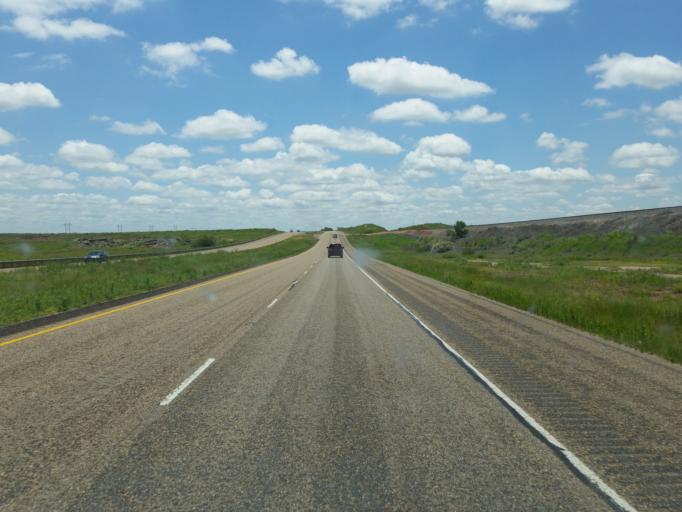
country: US
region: Texas
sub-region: Garza County
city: Post
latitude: 33.1128
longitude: -101.2729
